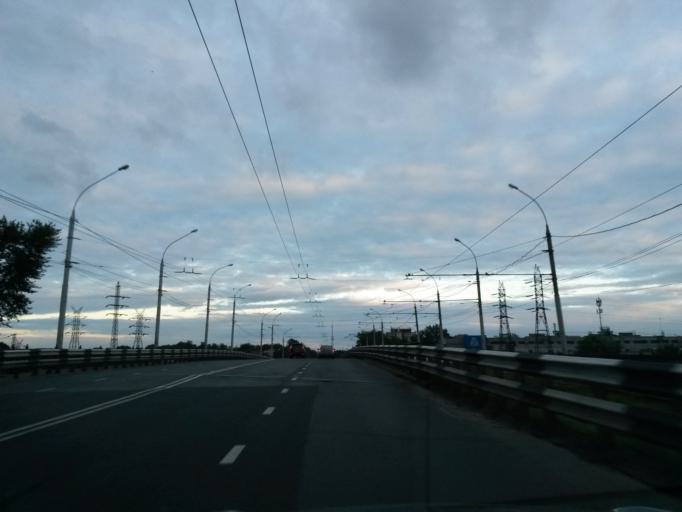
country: RU
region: Jaroslavl
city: Yaroslavl
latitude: 57.6443
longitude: 39.8532
